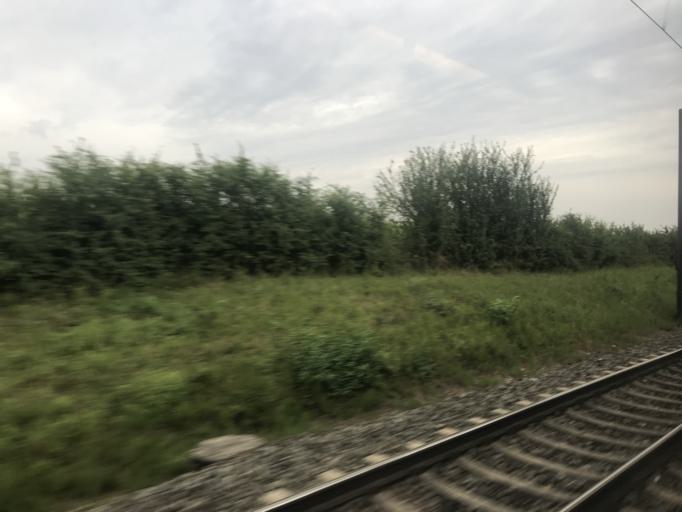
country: DE
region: Bavaria
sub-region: Regierungsbezirk Unterfranken
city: Bergrheinfeld
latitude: 50.0304
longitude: 10.1923
